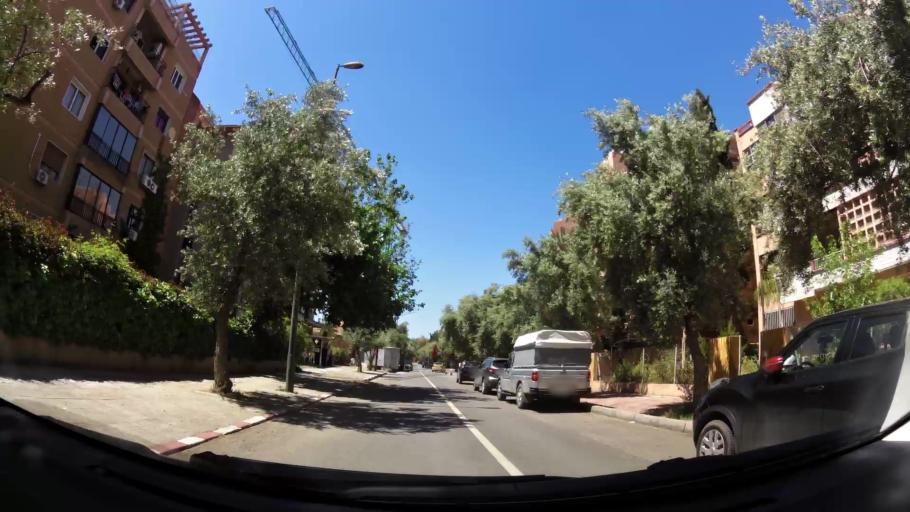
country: MA
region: Marrakech-Tensift-Al Haouz
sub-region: Marrakech
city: Marrakesh
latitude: 31.6256
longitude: -8.0029
